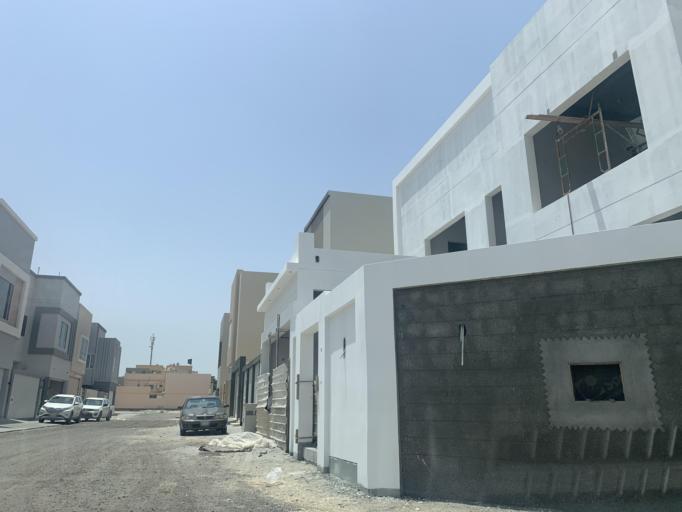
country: BH
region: Central Governorate
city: Madinat Hamad
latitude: 26.1488
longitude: 50.5040
